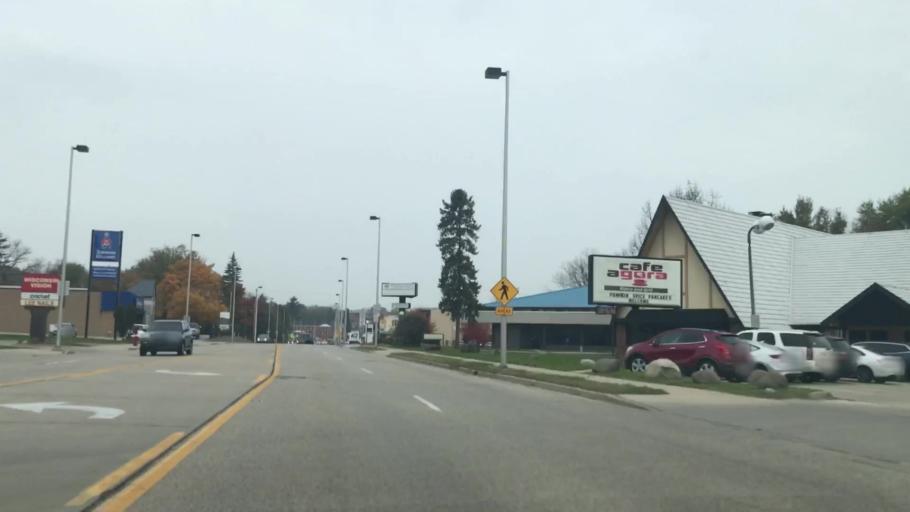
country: US
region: Wisconsin
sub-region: Waukesha County
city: Menomonee Falls
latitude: 43.1721
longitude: -88.1083
